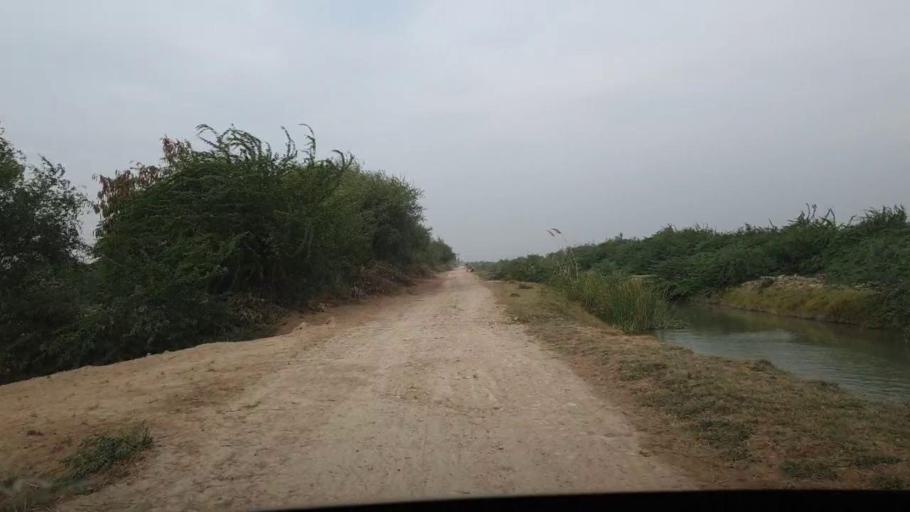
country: PK
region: Sindh
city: Chuhar Jamali
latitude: 24.4077
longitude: 67.9527
